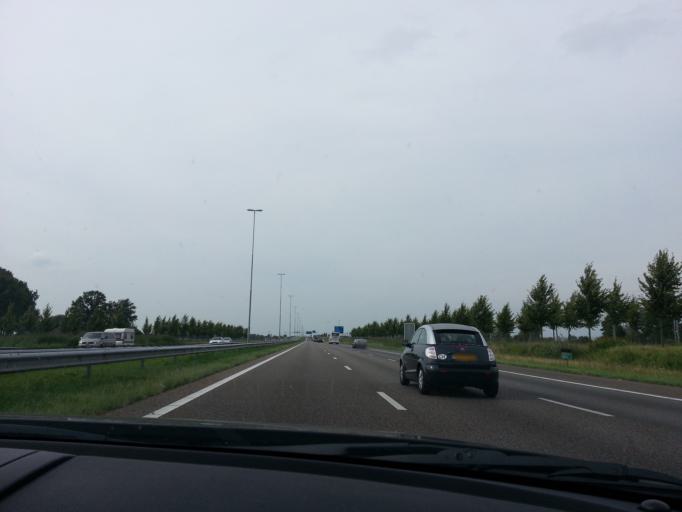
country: NL
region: North Brabant
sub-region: Gemeente Breda
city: Breda
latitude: 51.6288
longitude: 4.7042
